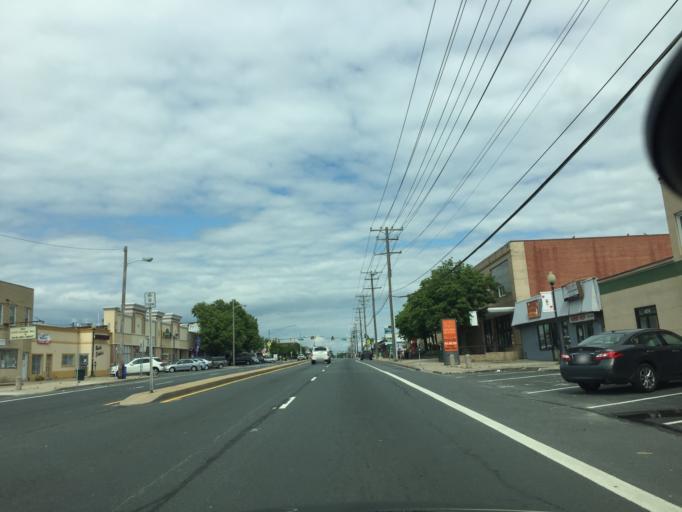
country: US
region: Maryland
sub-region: Baltimore County
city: Essex
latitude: 39.3074
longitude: -76.4780
